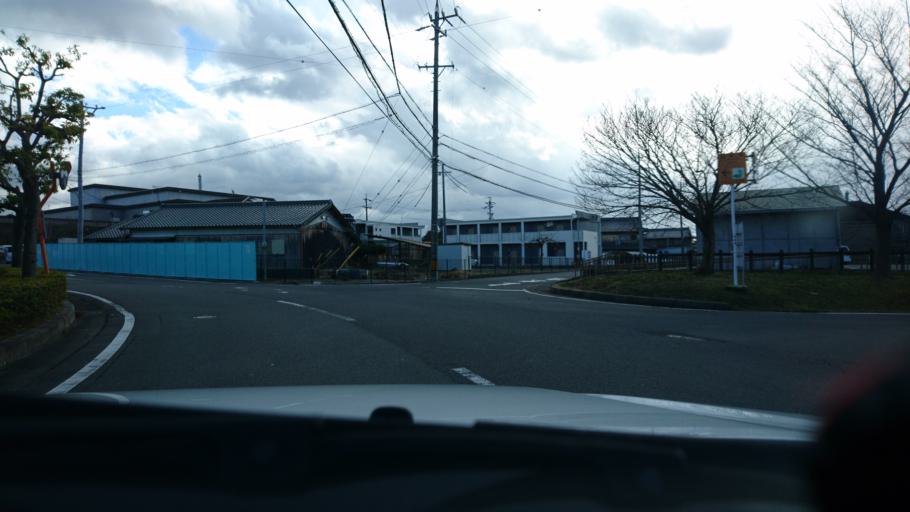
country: JP
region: Mie
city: Ueno-ebisumachi
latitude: 34.7569
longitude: 136.1557
